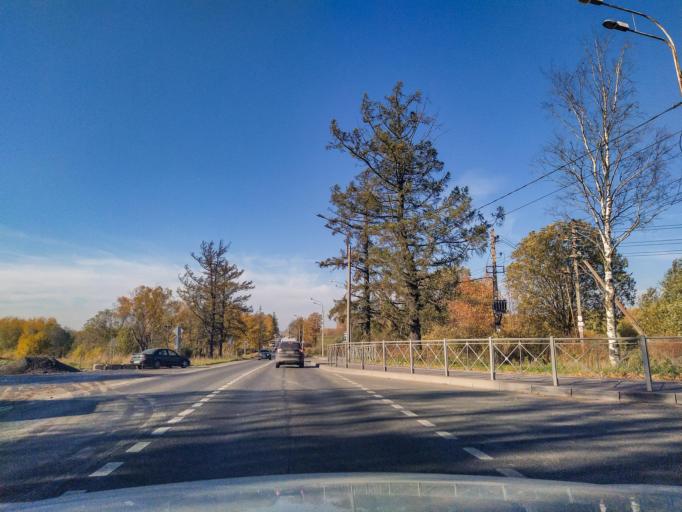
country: RU
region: St.-Petersburg
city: Aleksandrovskaya
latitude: 59.7075
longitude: 30.3317
